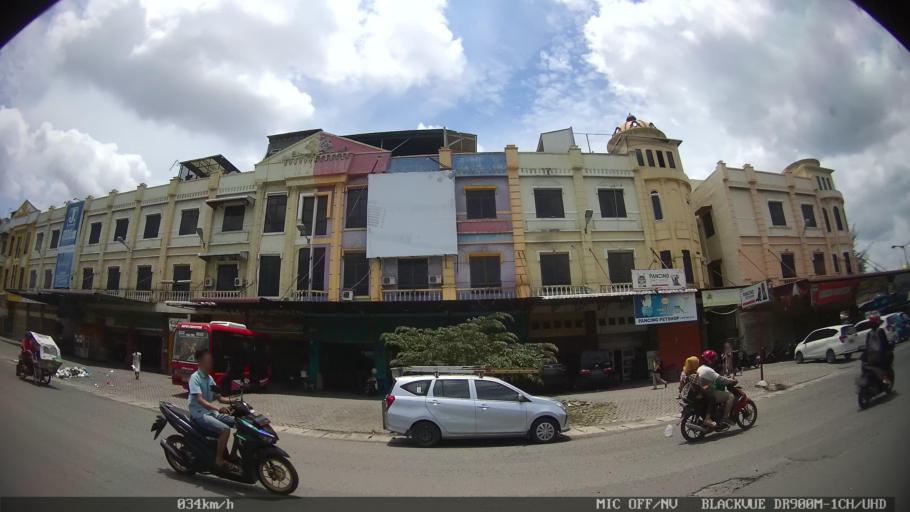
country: ID
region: North Sumatra
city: Medan
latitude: 3.6066
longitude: 98.7099
